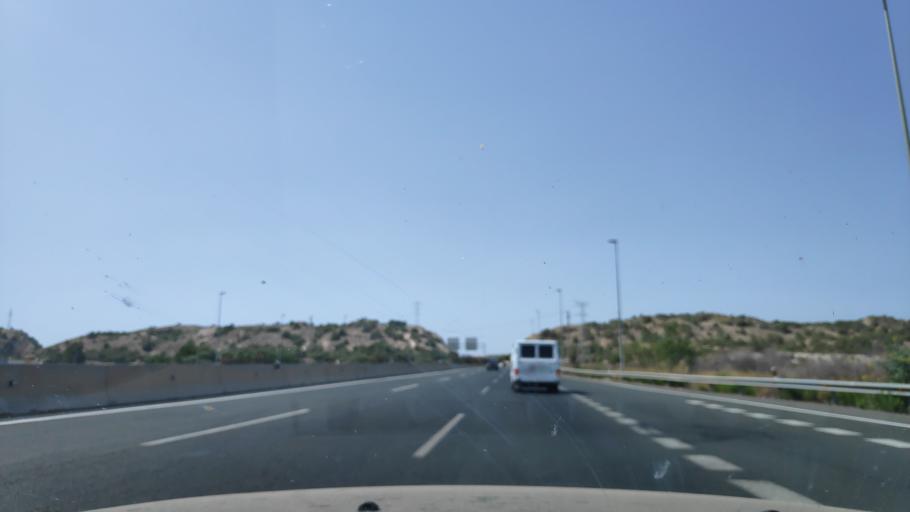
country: ES
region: Murcia
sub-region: Murcia
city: Murcia
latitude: 37.8679
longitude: -1.1230
